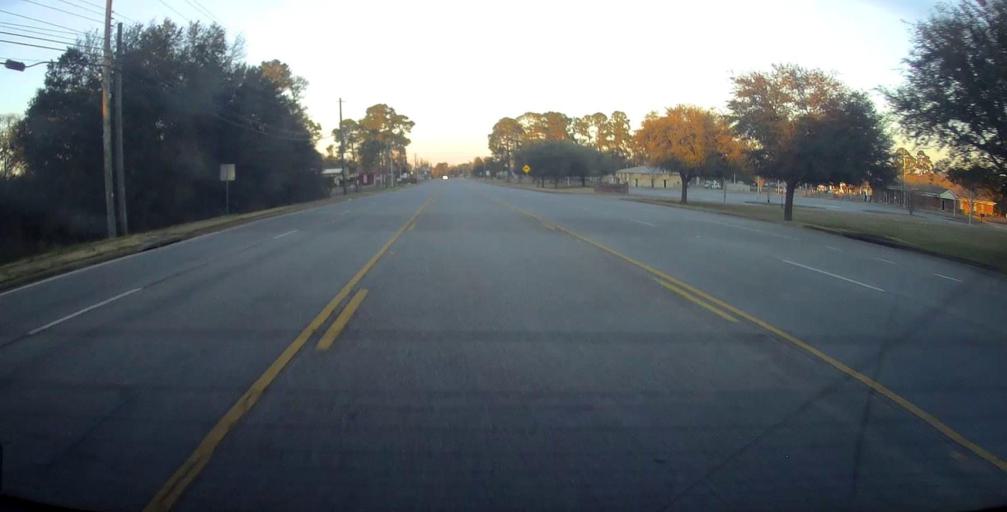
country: US
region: Georgia
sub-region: Dougherty County
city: Albany
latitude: 31.5499
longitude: -84.1739
